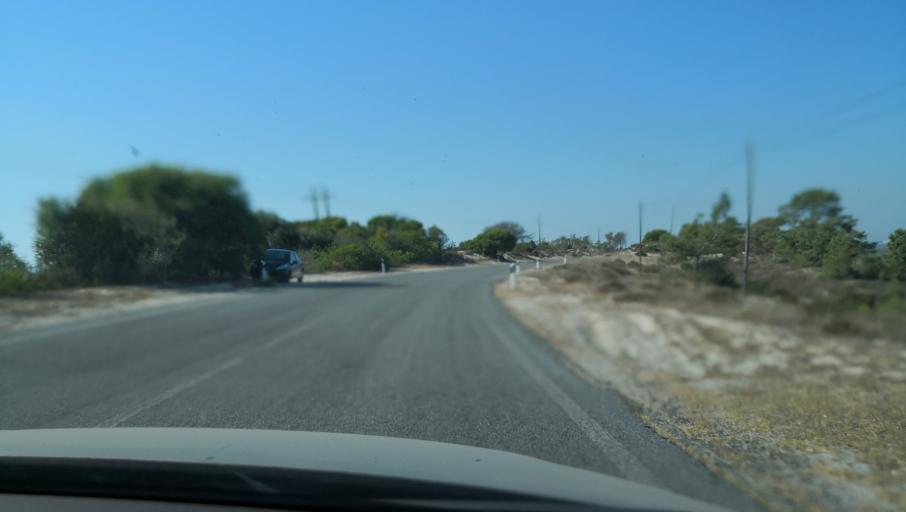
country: PT
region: Setubal
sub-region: Setubal
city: Setubal
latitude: 38.4194
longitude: -8.8197
